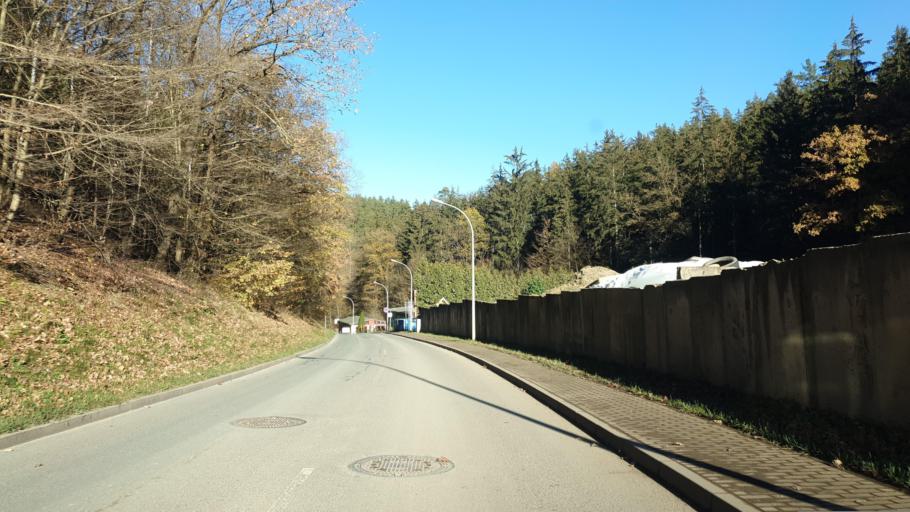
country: DE
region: Thuringia
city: Greiz
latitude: 50.6526
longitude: 12.1742
